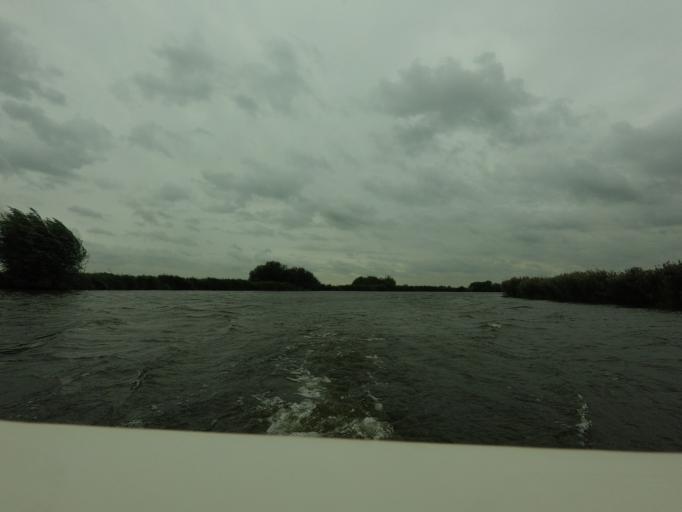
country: NL
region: Friesland
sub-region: Gemeente Boarnsterhim
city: Aldeboarn
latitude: 53.0985
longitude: 5.9031
